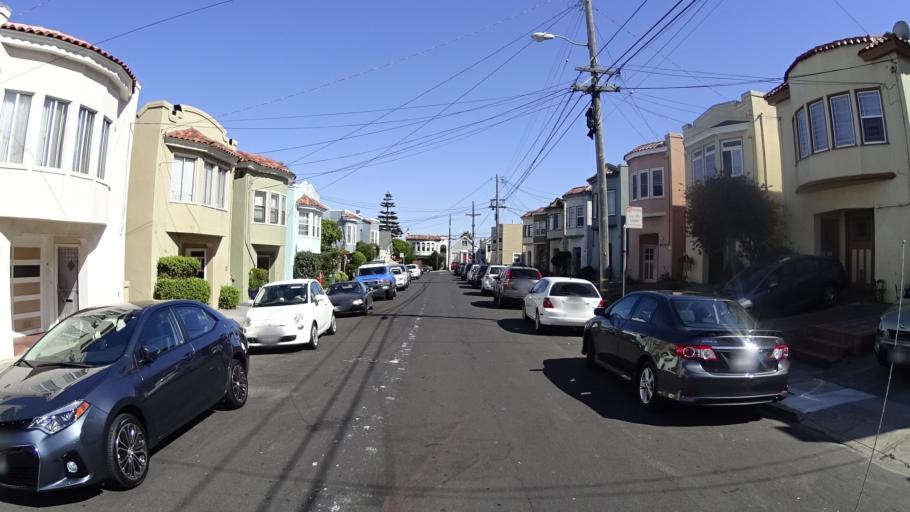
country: US
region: California
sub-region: San Mateo County
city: Daly City
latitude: 37.7074
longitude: -122.4506
